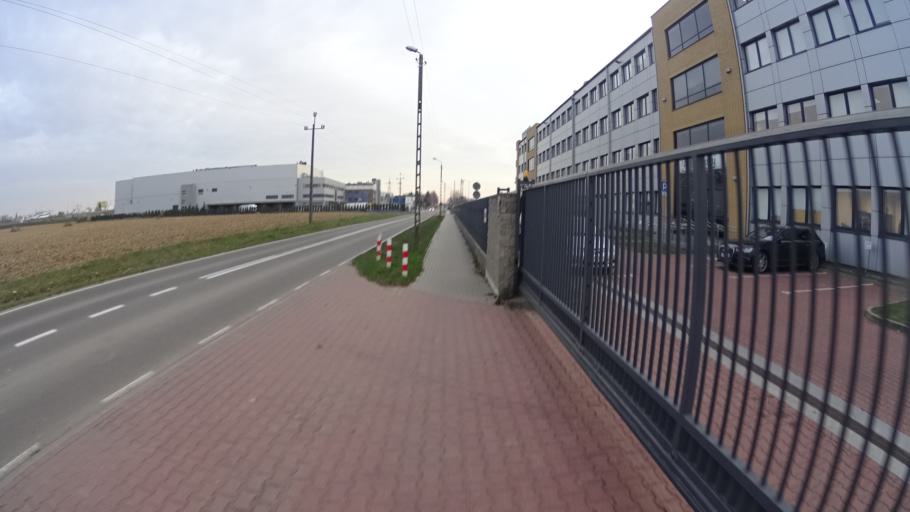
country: PL
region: Masovian Voivodeship
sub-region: Powiat warszawski zachodni
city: Babice
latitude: 52.2197
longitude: 20.8598
